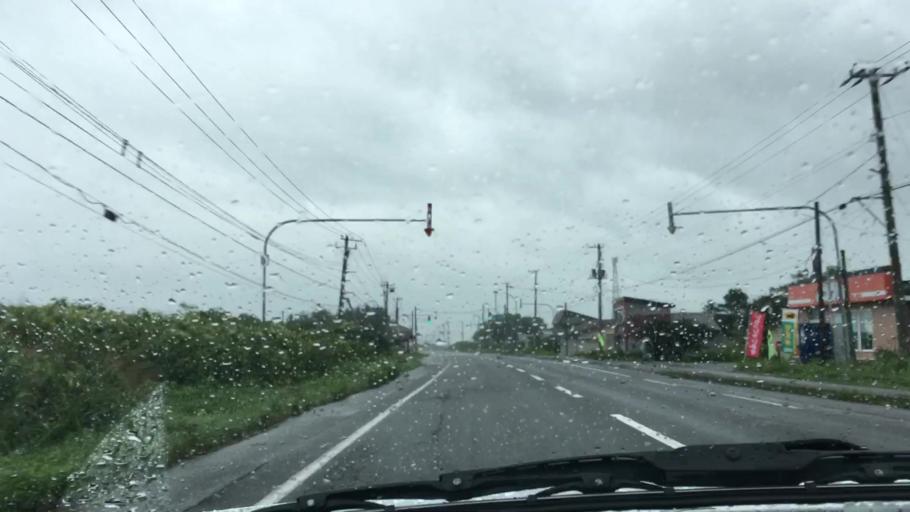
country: JP
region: Hokkaido
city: Nanae
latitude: 42.3157
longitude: 140.2741
